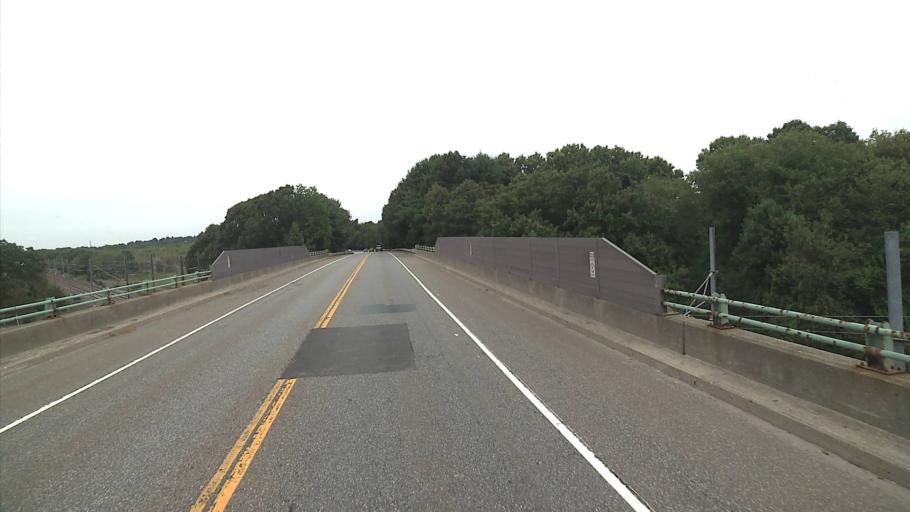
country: US
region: Connecticut
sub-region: Middlesex County
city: Old Saybrook Center
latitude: 41.3046
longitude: -72.3292
